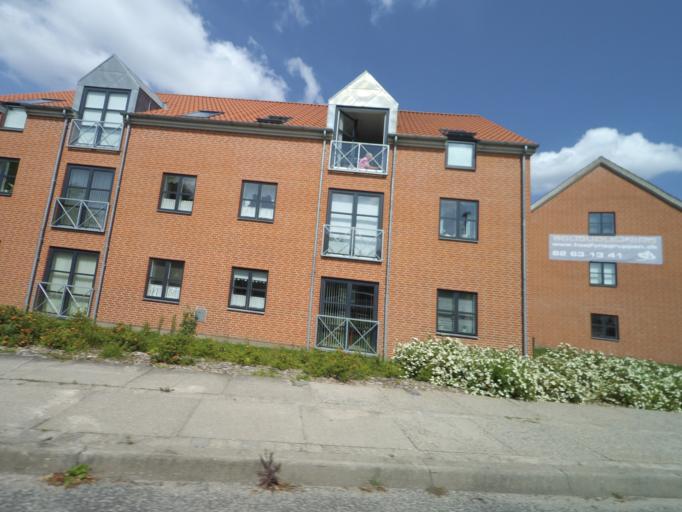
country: DK
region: South Denmark
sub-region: Assens Kommune
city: Arup
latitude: 55.3771
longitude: 10.0464
